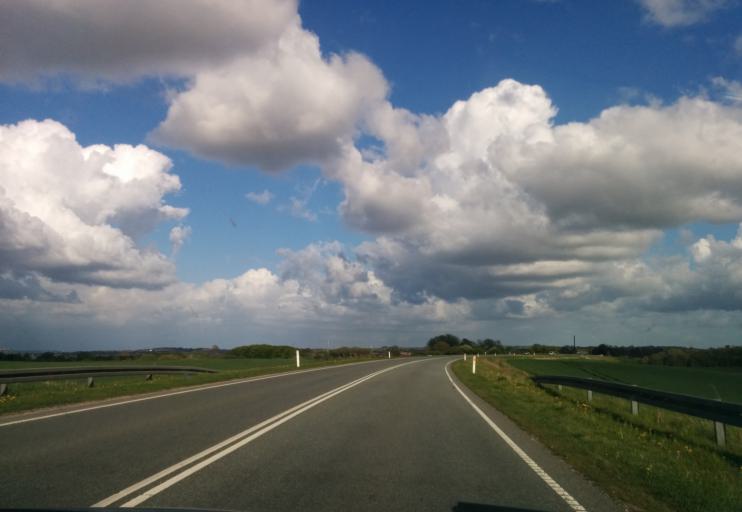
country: DK
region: Central Jutland
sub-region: Arhus Kommune
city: Stavtrup
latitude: 56.1174
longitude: 10.1051
